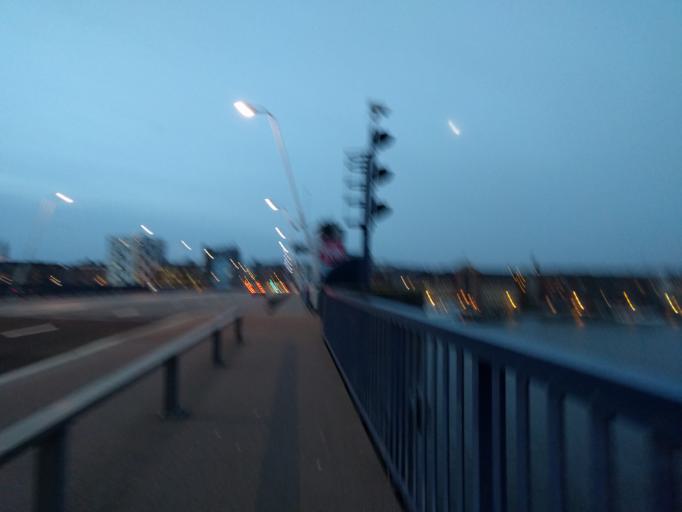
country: DK
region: North Denmark
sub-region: Alborg Kommune
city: Aalborg
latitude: 57.0546
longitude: 9.9194
